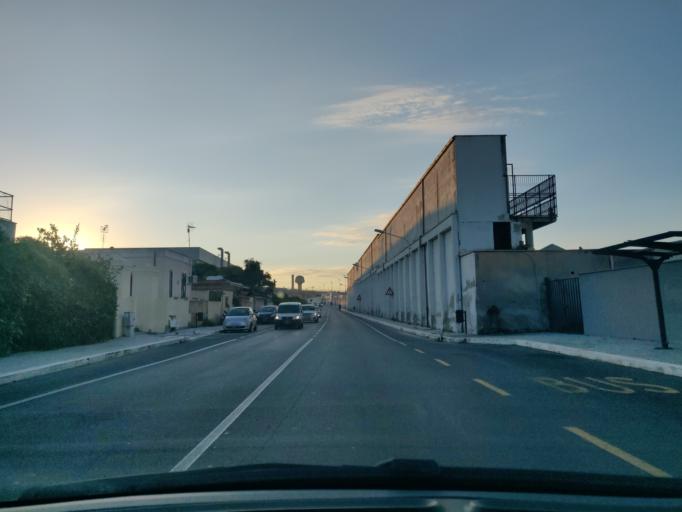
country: IT
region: Latium
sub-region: Citta metropolitana di Roma Capitale
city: Civitavecchia
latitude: 42.1065
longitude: 11.7824
